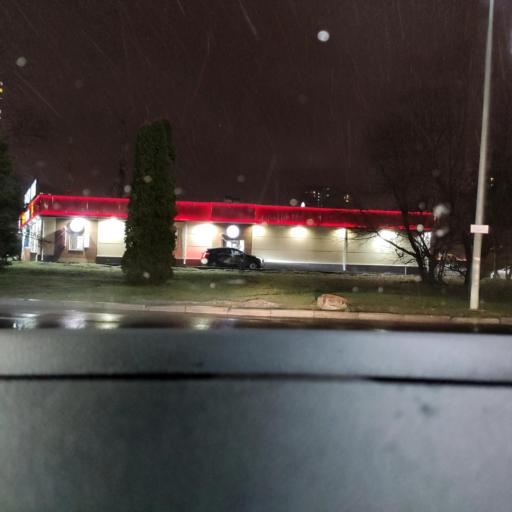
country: RU
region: Moscow
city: Nikol'skoye
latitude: 55.6785
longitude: 37.4813
